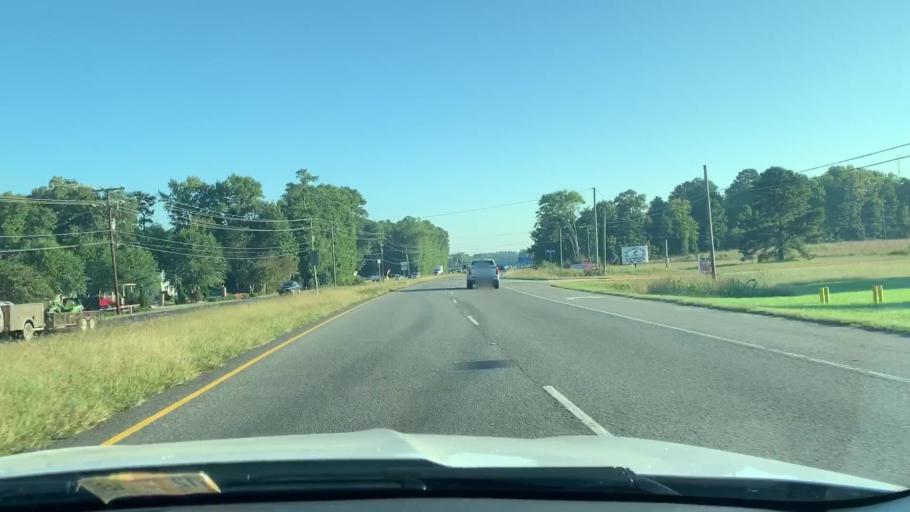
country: US
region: Virginia
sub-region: Gloucester County
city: Gloucester Courthouse
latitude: 37.3869
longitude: -76.5333
